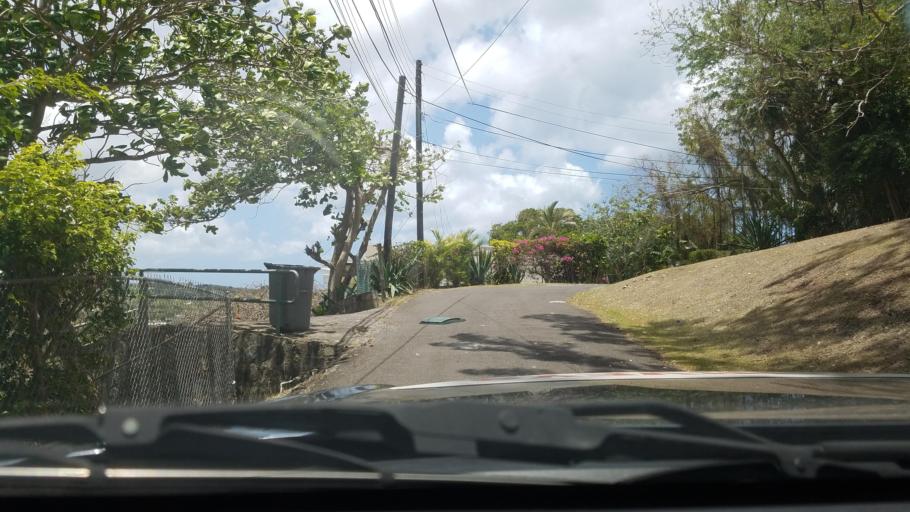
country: LC
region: Castries Quarter
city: Bisee
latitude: 14.0205
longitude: -60.9991
